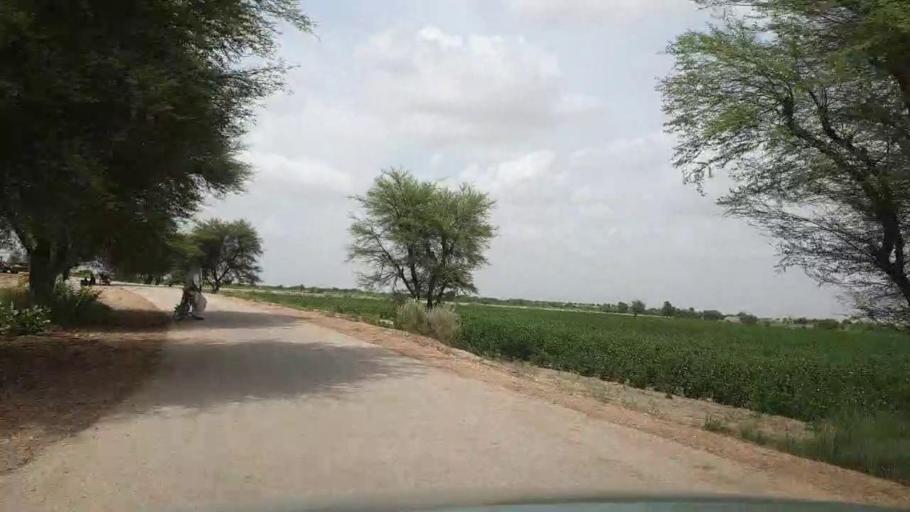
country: PK
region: Sindh
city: Kot Diji
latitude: 27.2282
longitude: 69.0891
